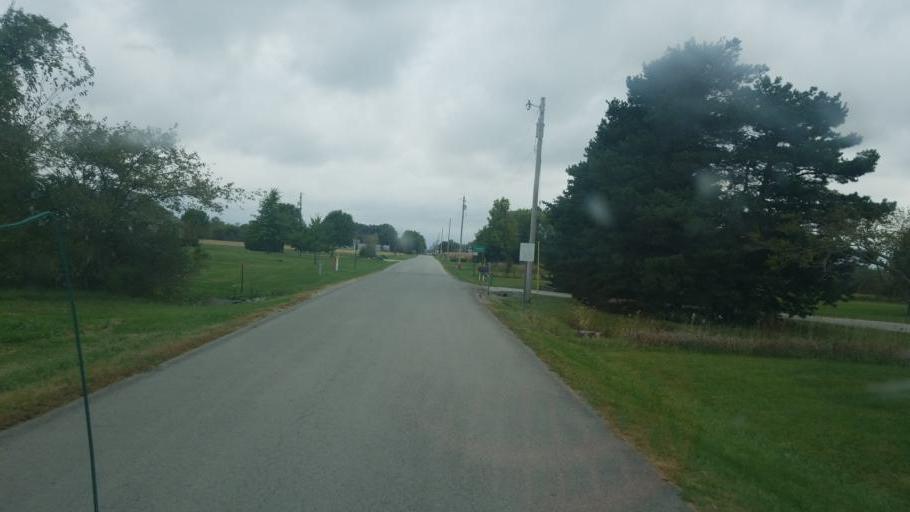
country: US
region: Ohio
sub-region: Seneca County
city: Fostoria
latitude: 41.1006
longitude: -83.5164
